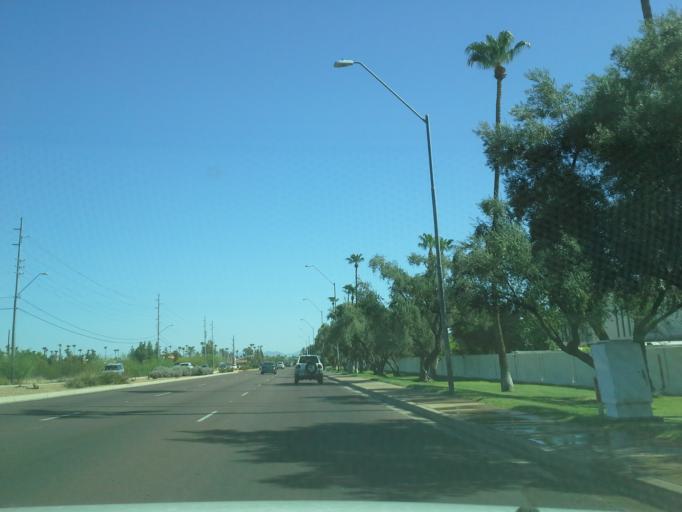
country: US
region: Arizona
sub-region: Maricopa County
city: Paradise Valley
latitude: 33.5350
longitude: -111.9256
